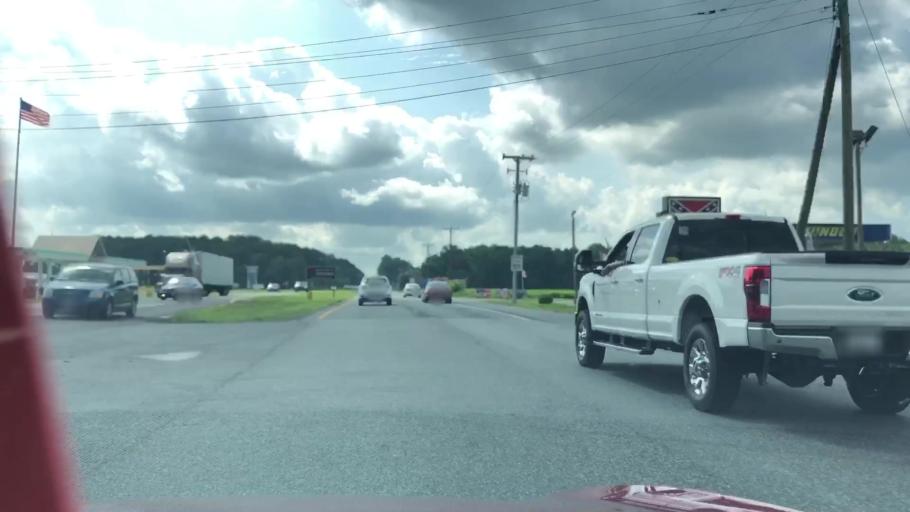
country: US
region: Maryland
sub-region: Worcester County
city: Pocomoke City
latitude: 38.0016
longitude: -75.5421
